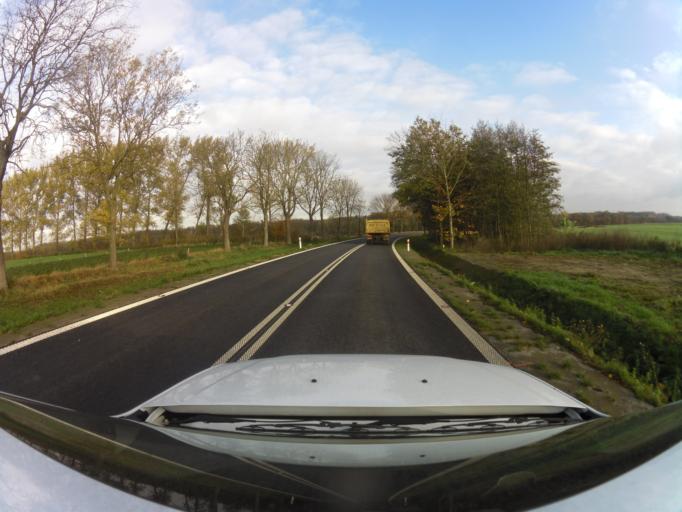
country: PL
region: West Pomeranian Voivodeship
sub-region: Powiat gryficki
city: Gryfice
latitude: 53.9603
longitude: 15.2274
